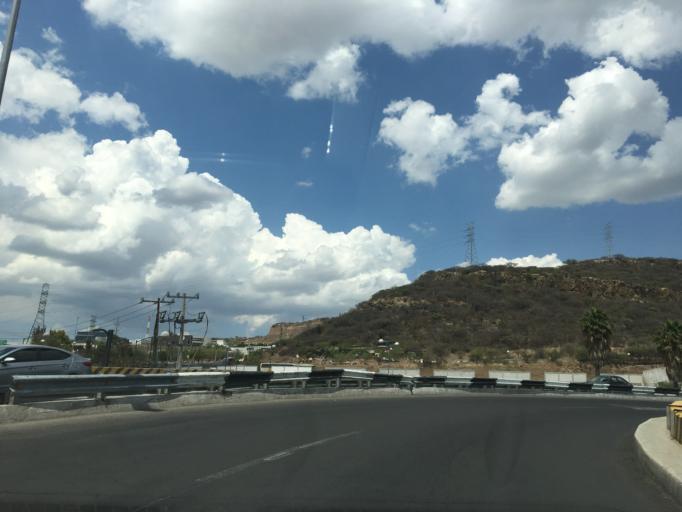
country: MX
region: Queretaro
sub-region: Queretaro
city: Santiago de Queretaro
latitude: 20.5807
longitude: -100.3603
